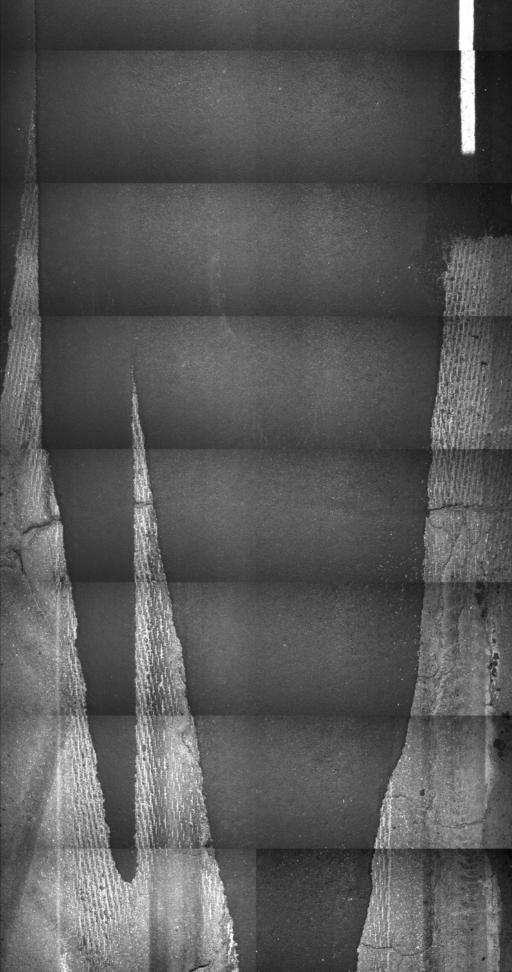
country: US
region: Vermont
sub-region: Orange County
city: Randolph
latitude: 43.9015
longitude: -72.6567
